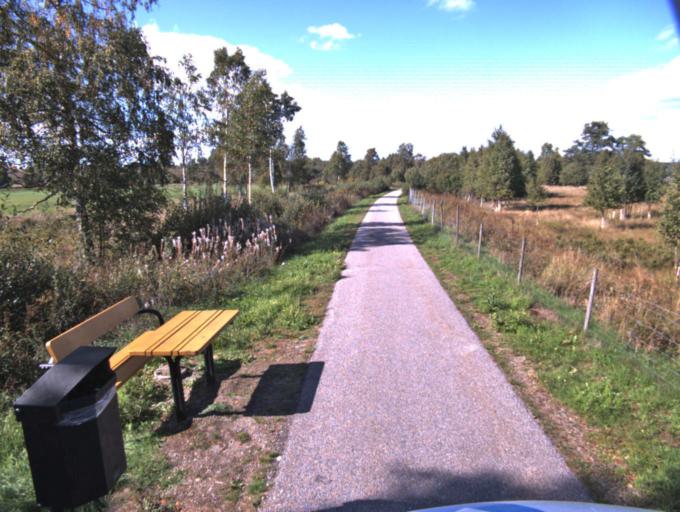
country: SE
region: Vaestra Goetaland
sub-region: Ulricehamns Kommun
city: Ulricehamn
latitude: 57.8392
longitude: 13.3056
